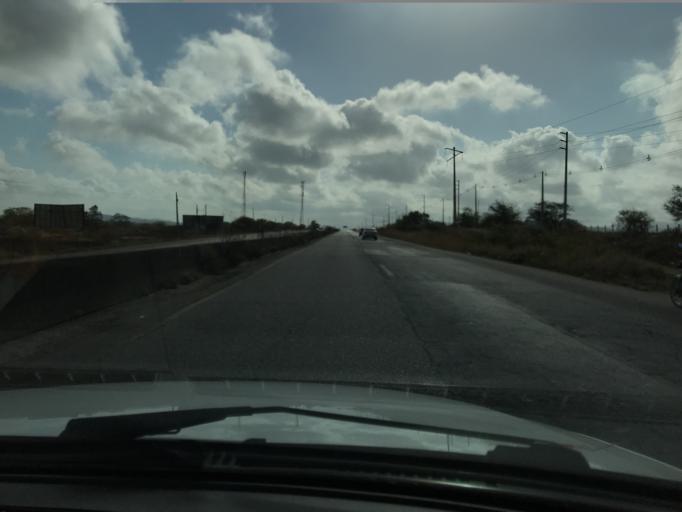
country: BR
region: Pernambuco
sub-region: Gravata
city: Gravata
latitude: -8.2175
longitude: -35.6560
